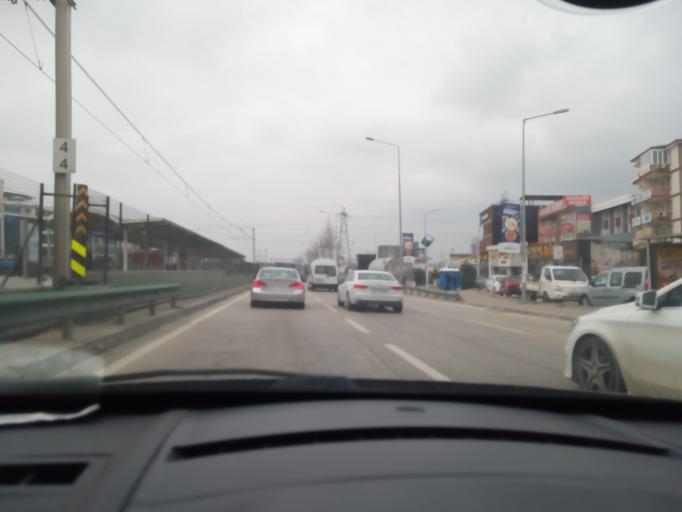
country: TR
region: Bursa
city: Niluefer
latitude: 40.2366
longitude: 28.9762
